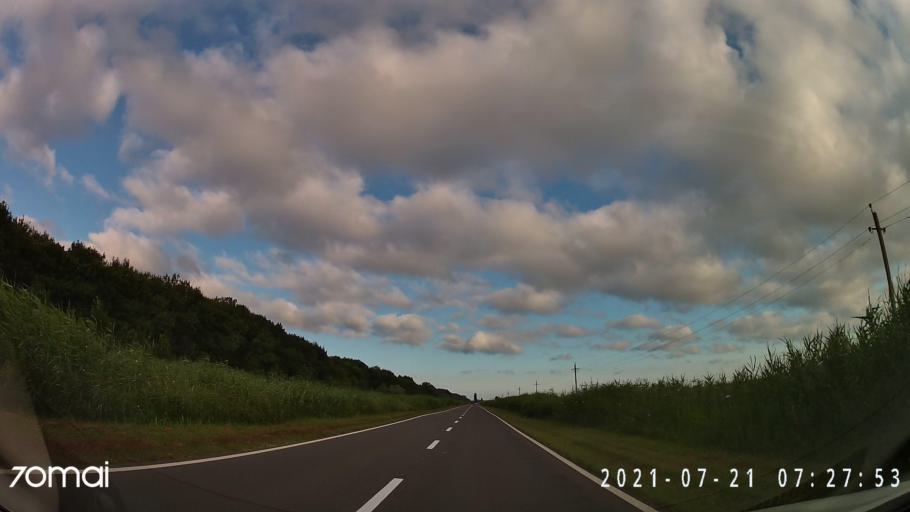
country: RO
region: Tulcea
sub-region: Oras Isaccea
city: Isaccea
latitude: 45.3068
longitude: 28.4063
